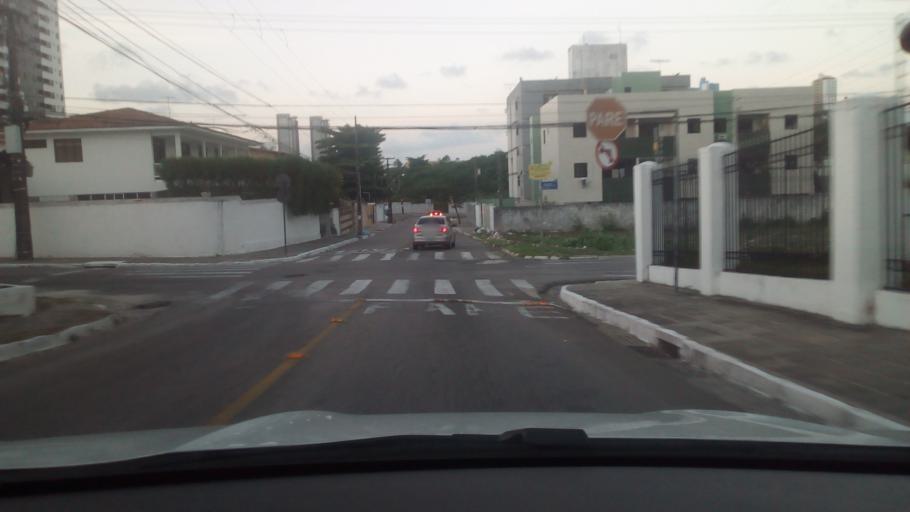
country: BR
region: Paraiba
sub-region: Joao Pessoa
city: Joao Pessoa
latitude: -7.1147
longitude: -34.8457
